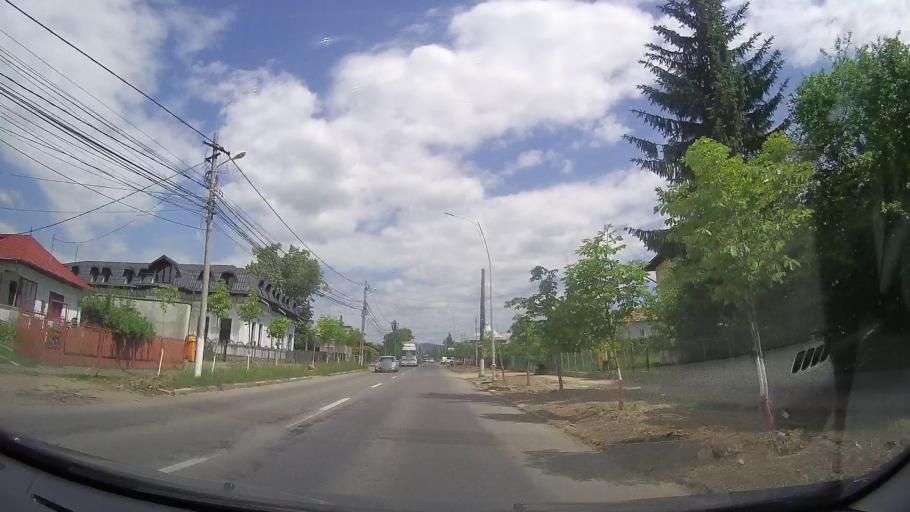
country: RO
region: Prahova
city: Valenii de Munte
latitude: 45.1962
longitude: 26.0432
